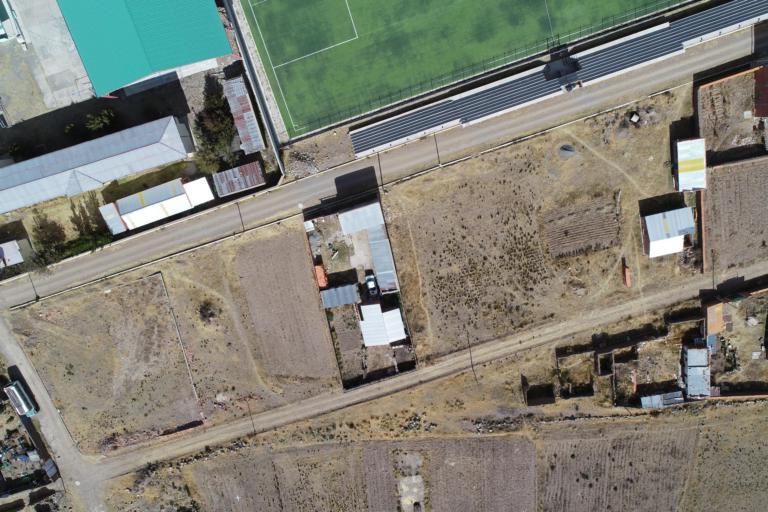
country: BO
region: La Paz
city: Achacachi
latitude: -15.8954
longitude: -68.9076
